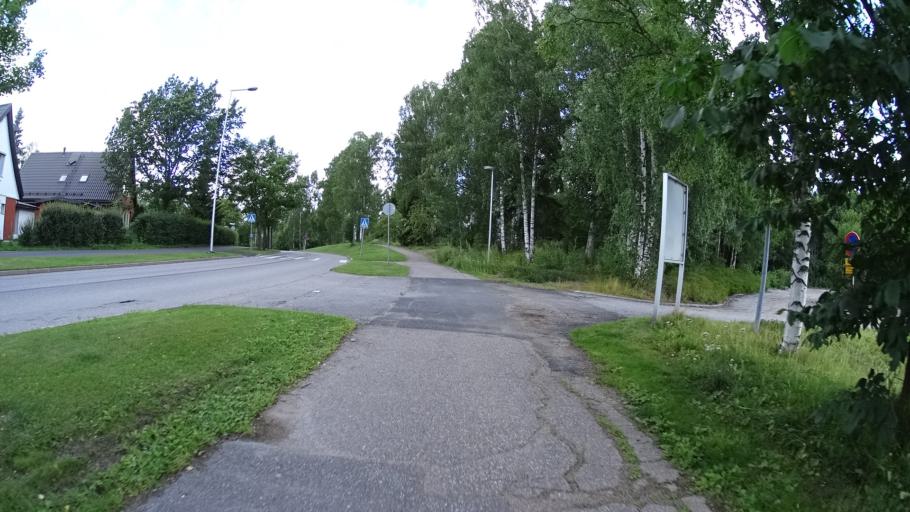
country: FI
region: Uusimaa
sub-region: Helsinki
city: Kilo
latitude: 60.2695
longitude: 24.8148
